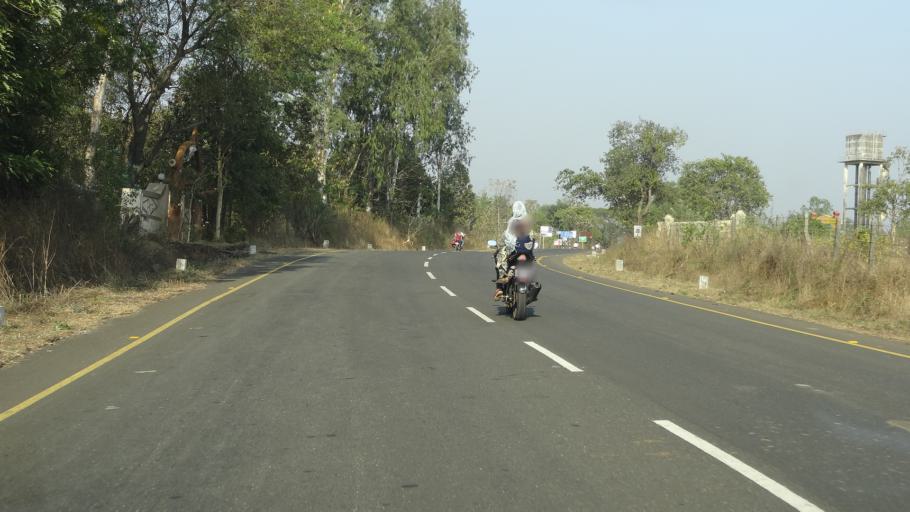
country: IN
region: Maharashtra
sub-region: Raigarh
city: Karjat
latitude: 18.9712
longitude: 73.3948
